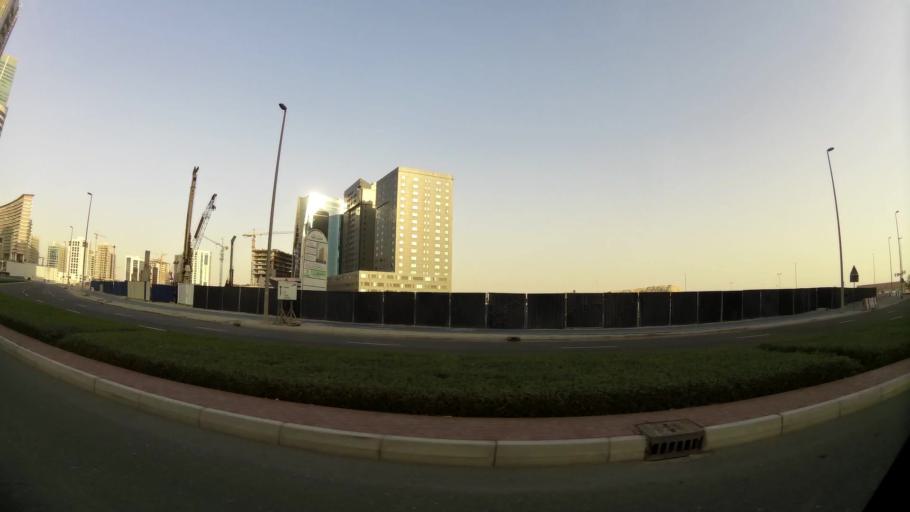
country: AE
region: Dubai
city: Dubai
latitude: 25.1803
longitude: 55.2649
